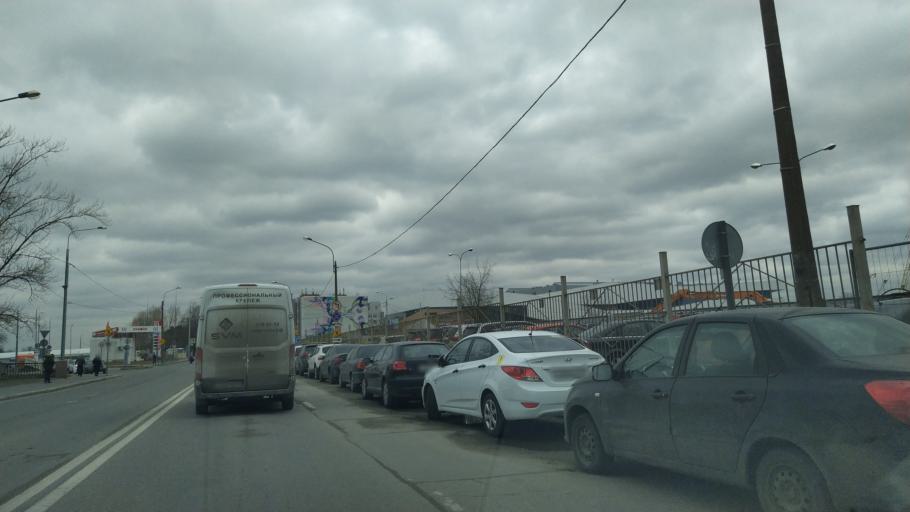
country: RU
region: St.-Petersburg
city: Centralniy
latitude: 59.9364
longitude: 30.4161
